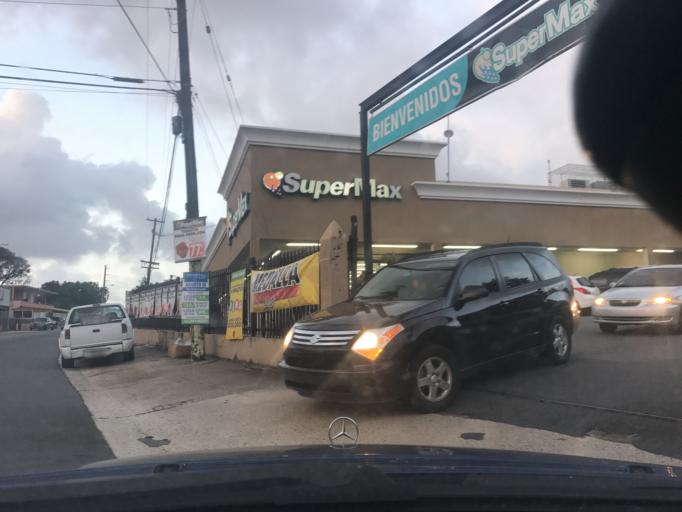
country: PR
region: Bayamon
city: Bayamon
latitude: 18.3707
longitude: -66.1678
